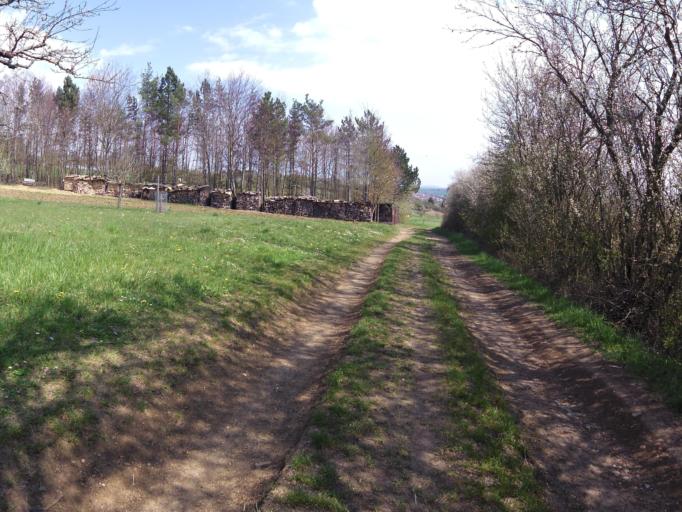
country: DE
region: Bavaria
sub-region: Regierungsbezirk Unterfranken
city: Rimpar
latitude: 49.8639
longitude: 9.9403
